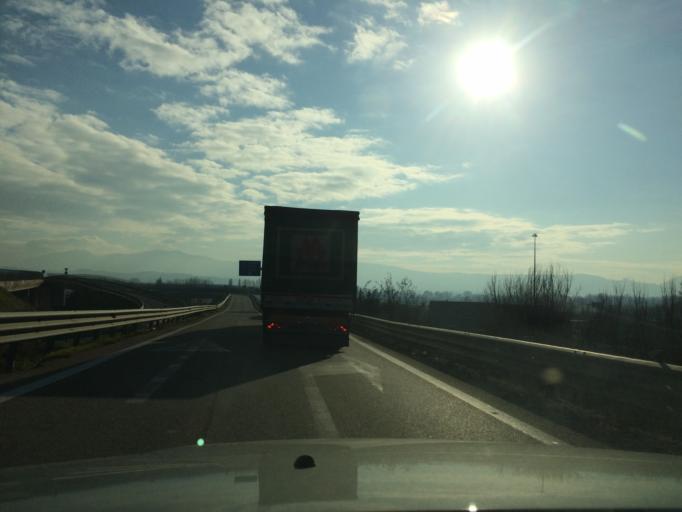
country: IT
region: Umbria
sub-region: Provincia di Terni
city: San Gemini
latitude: 42.5712
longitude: 12.5752
